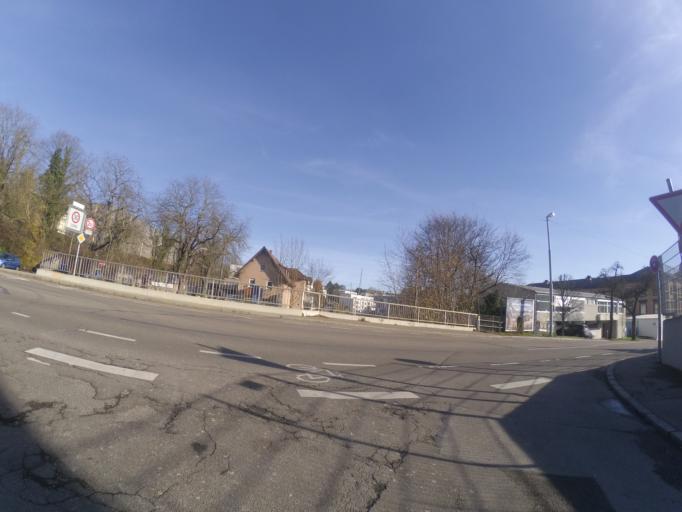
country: DE
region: Baden-Wuerttemberg
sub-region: Tuebingen Region
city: Ulm
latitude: 48.4074
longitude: 9.9918
